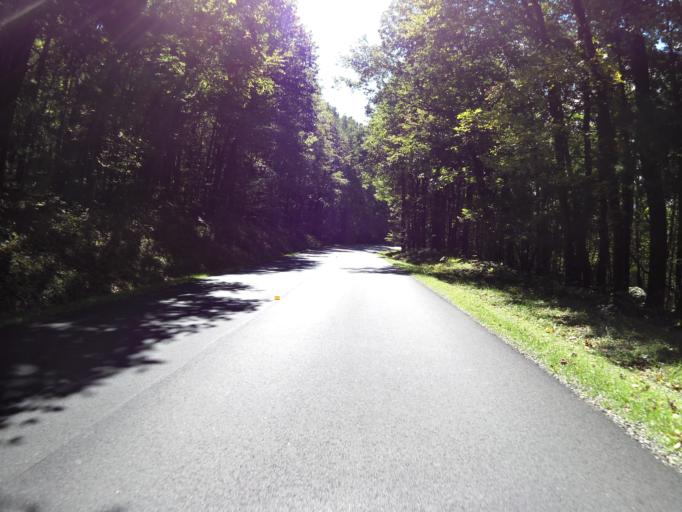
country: US
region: Virginia
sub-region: Page County
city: Luray
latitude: 38.6843
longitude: -78.3259
